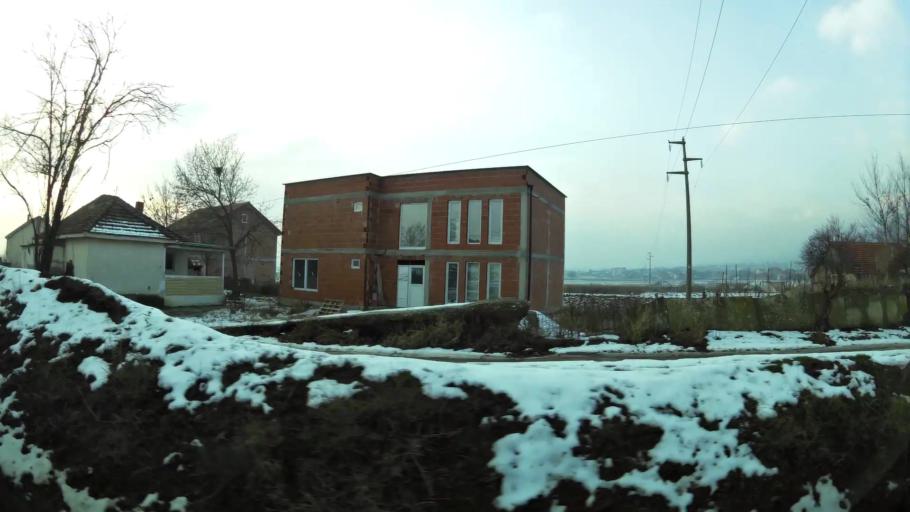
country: MK
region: Aracinovo
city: Arachinovo
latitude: 42.0201
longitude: 21.5599
